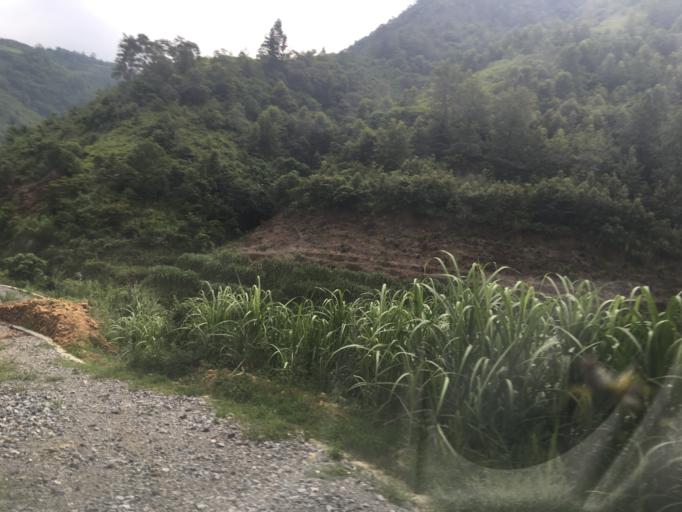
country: CN
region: Guangxi Zhuangzu Zizhiqu
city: Xinzhou
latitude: 25.1700
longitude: 105.6978
